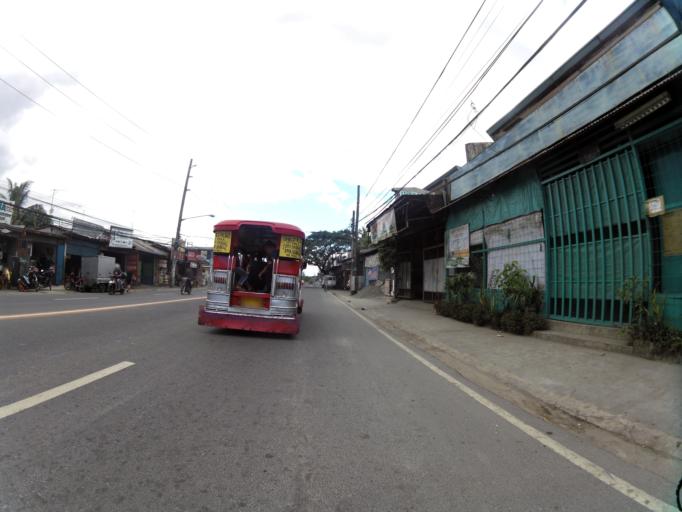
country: PH
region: Calabarzon
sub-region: Province of Rizal
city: Antipolo
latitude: 14.6304
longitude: 121.1190
